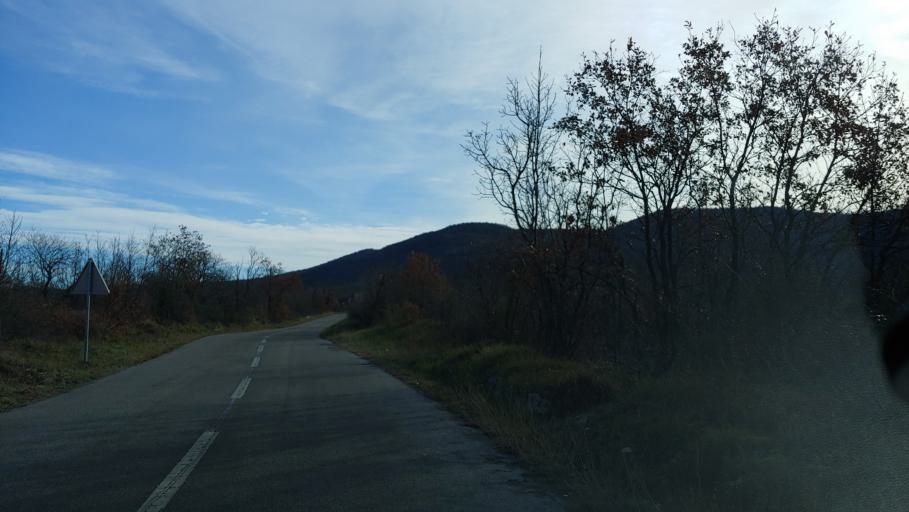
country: IT
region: Friuli Venezia Giulia
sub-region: Provincia di Trieste
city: Duino
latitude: 45.8132
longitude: 13.6054
